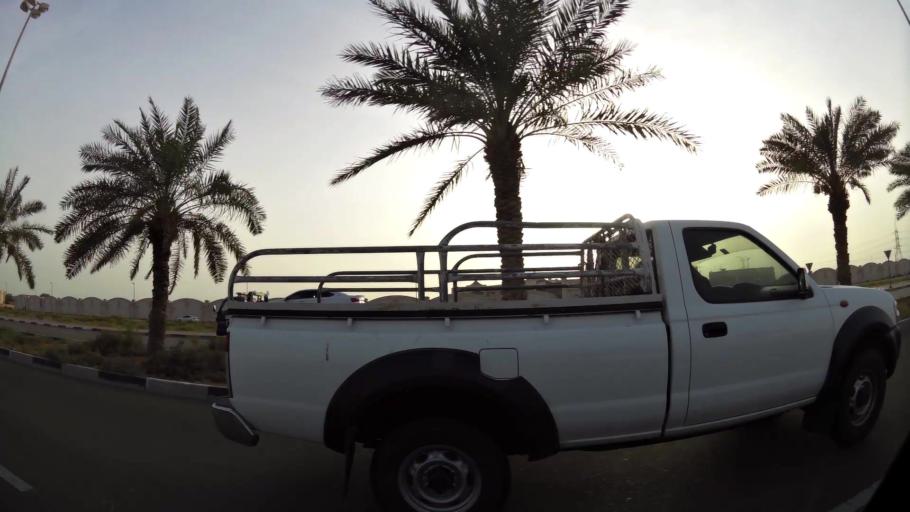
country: OM
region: Al Buraimi
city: Al Buraymi
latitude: 24.2712
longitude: 55.7206
